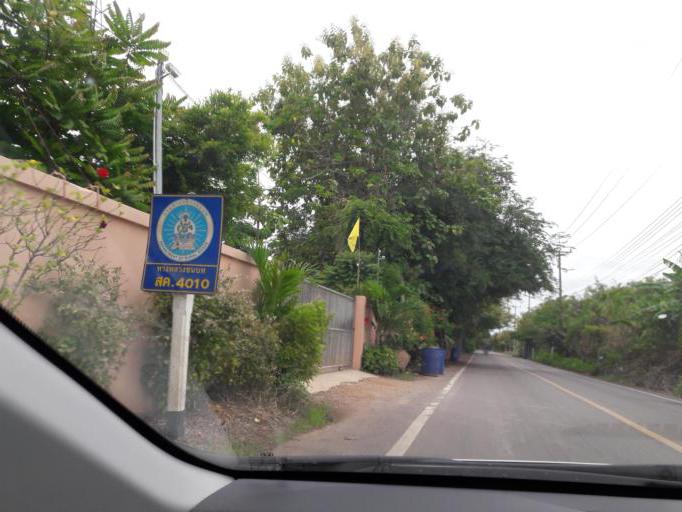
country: TH
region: Samut Sakhon
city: Ban Phaeo
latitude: 13.6235
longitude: 100.0201
